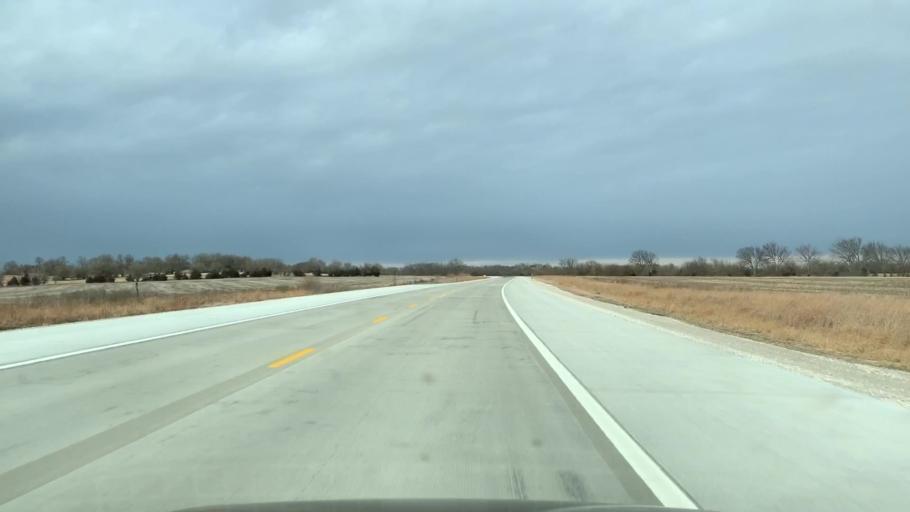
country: US
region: Kansas
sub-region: Allen County
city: Humboldt
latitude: 37.8562
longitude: -95.4080
